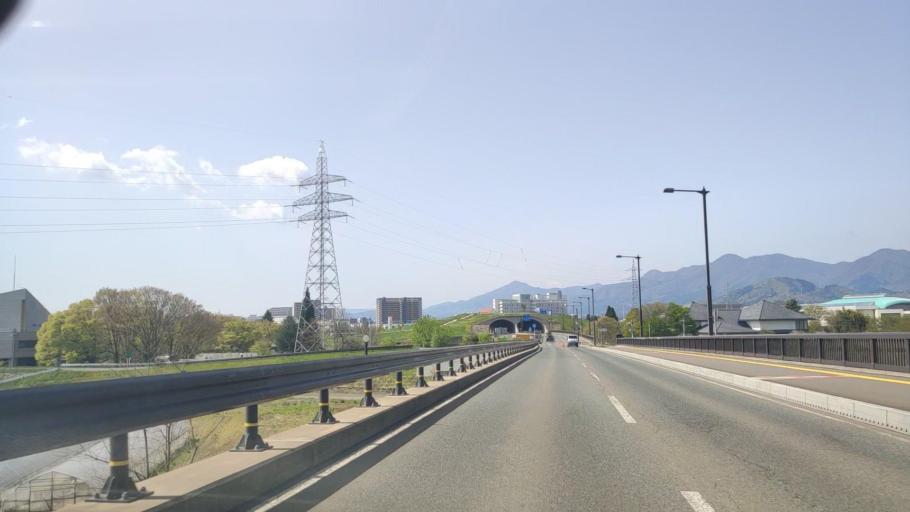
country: JP
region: Iwate
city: Morioka-shi
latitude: 39.6962
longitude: 141.1292
